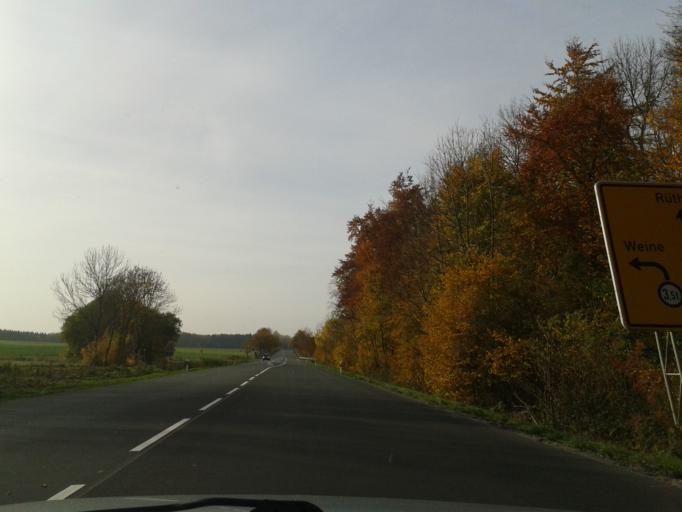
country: DE
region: North Rhine-Westphalia
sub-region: Regierungsbezirk Detmold
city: Buren
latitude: 51.5538
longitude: 8.5155
